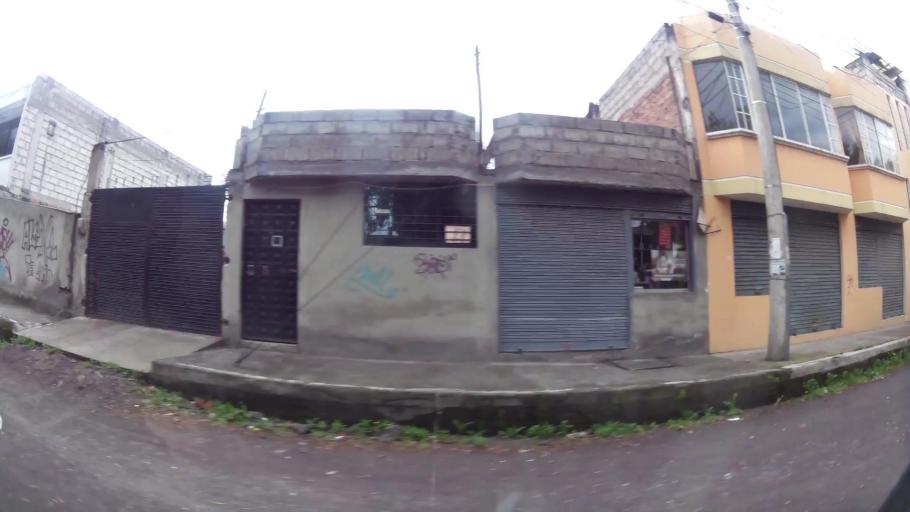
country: EC
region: Pichincha
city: Quito
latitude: -0.3099
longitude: -78.5542
